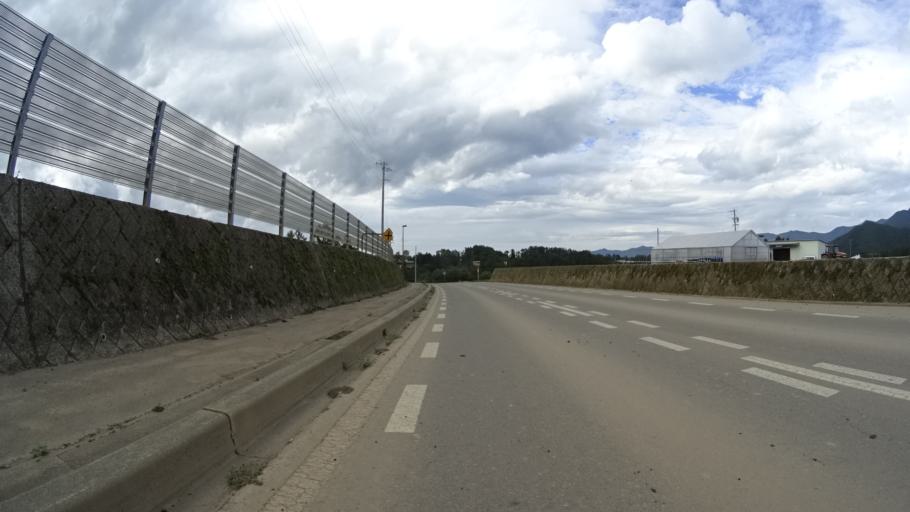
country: JP
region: Nagano
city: Saku
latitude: 35.9707
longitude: 138.5149
